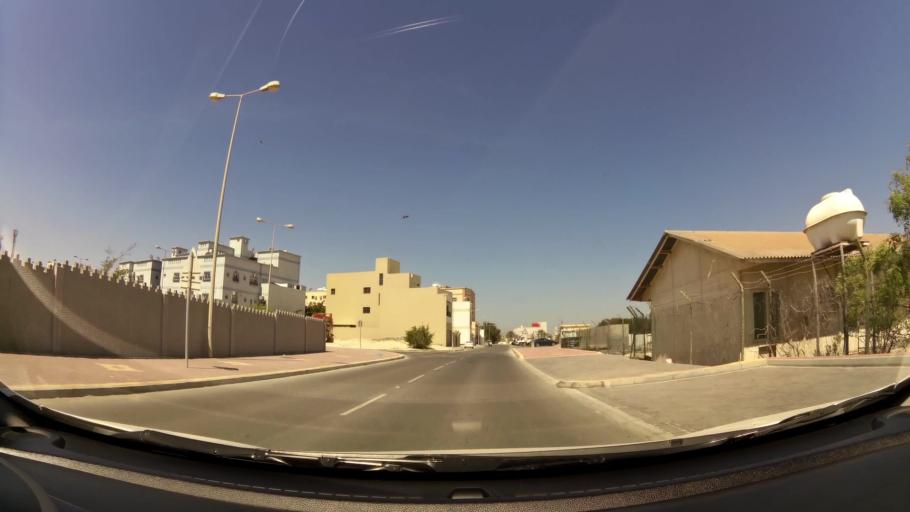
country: BH
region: Muharraq
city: Al Muharraq
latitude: 26.2697
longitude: 50.6126
